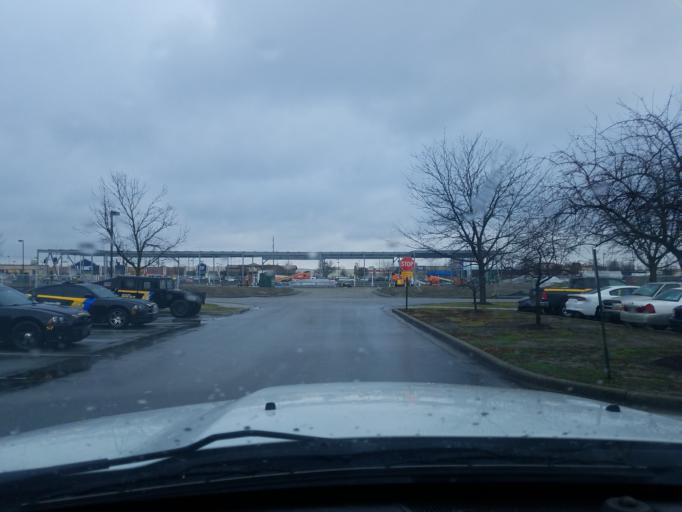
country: US
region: Indiana
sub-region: Clark County
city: Clarksville
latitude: 38.3294
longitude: -85.7619
